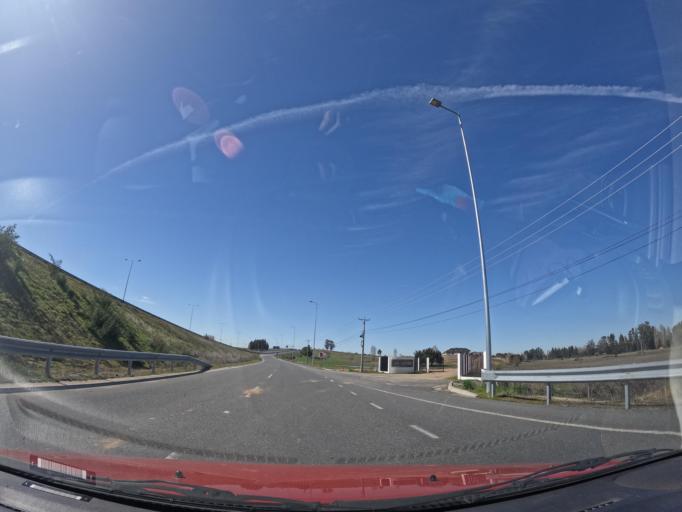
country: CL
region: Biobio
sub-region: Provincia de Biobio
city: Yumbel
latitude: -37.0010
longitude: -72.5611
